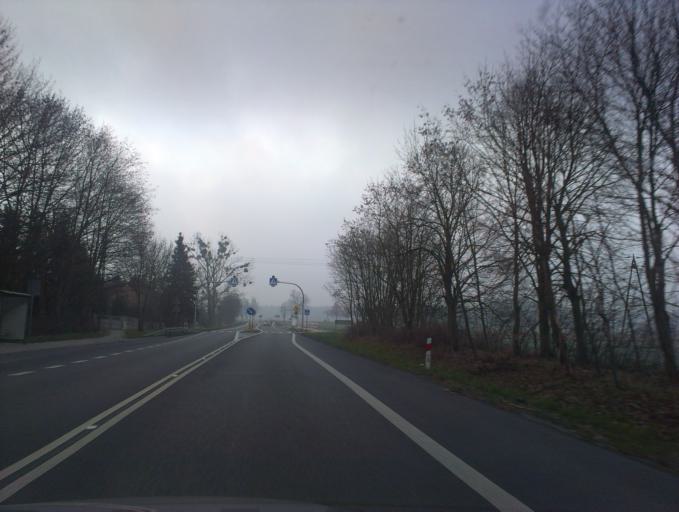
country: PL
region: Greater Poland Voivodeship
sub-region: Powiat chodzieski
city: Chodziez
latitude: 52.9546
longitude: 16.9397
